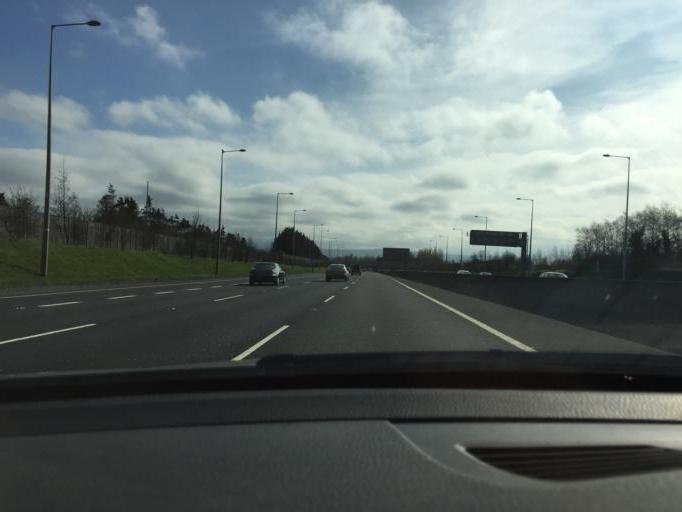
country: IE
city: Palmerstown
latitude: 53.3466
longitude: -6.3864
